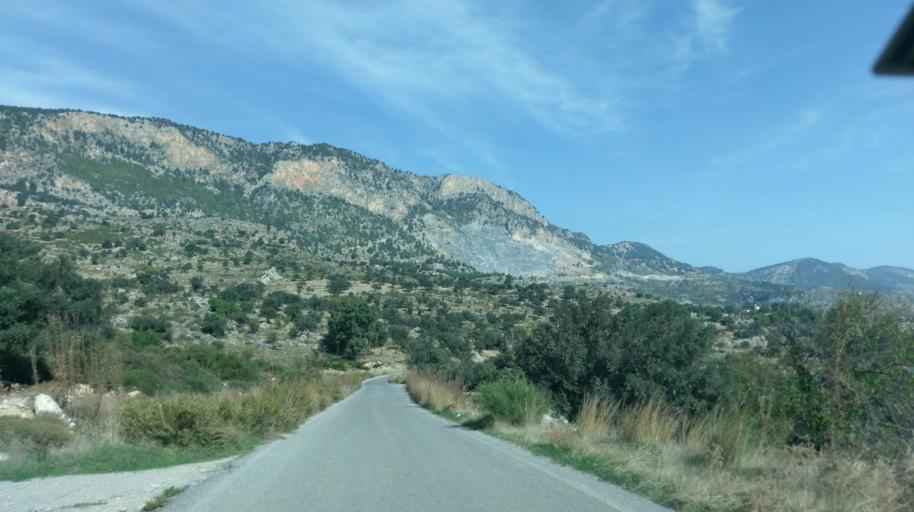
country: CY
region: Keryneia
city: Lapithos
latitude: 35.2988
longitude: 33.1648
